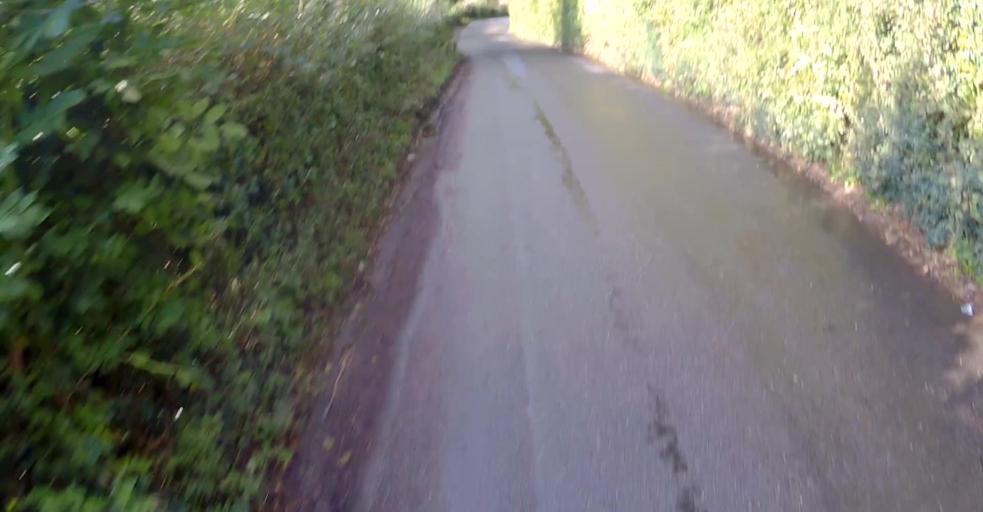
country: GB
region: England
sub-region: Surrey
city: Farnham
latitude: 51.2035
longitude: -0.8260
